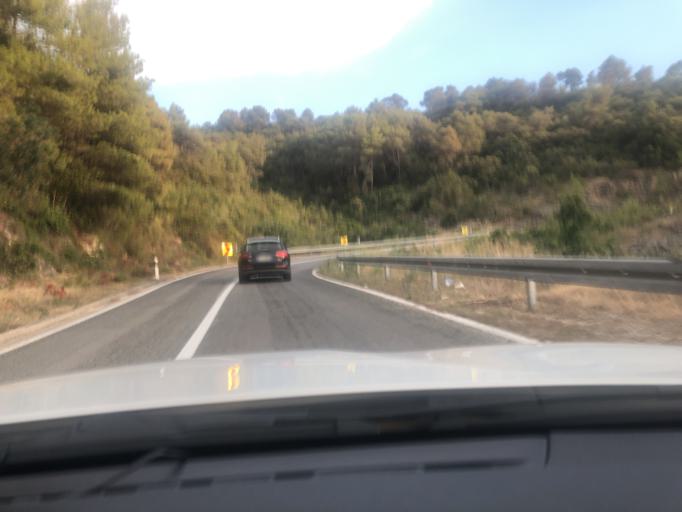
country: HR
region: Splitsko-Dalmatinska
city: Stari Grad
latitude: 43.1723
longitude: 16.5662
